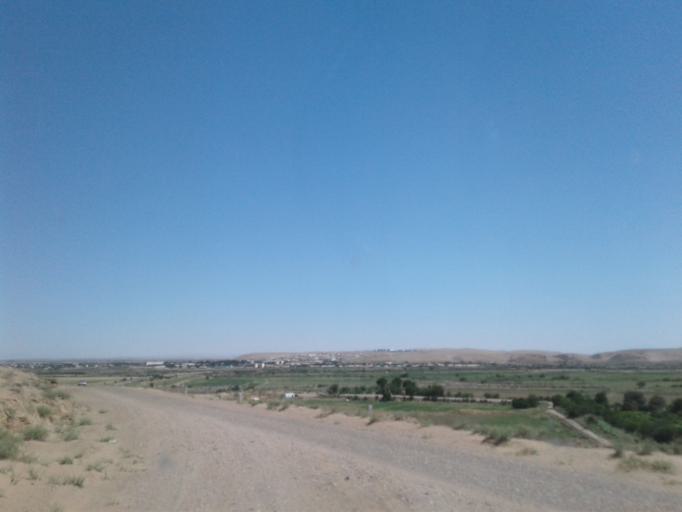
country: AF
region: Badghis
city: Bala Murghab
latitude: 35.9772
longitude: 62.8997
